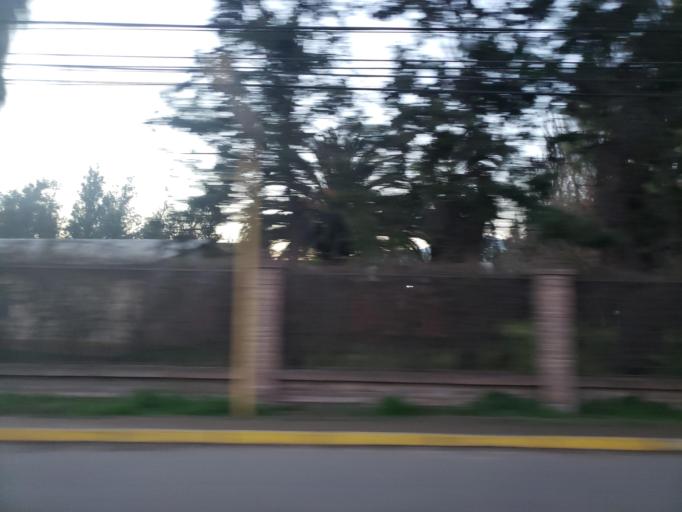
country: CL
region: Santiago Metropolitan
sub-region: Provincia de Talagante
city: El Monte
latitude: -33.6810
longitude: -70.9603
